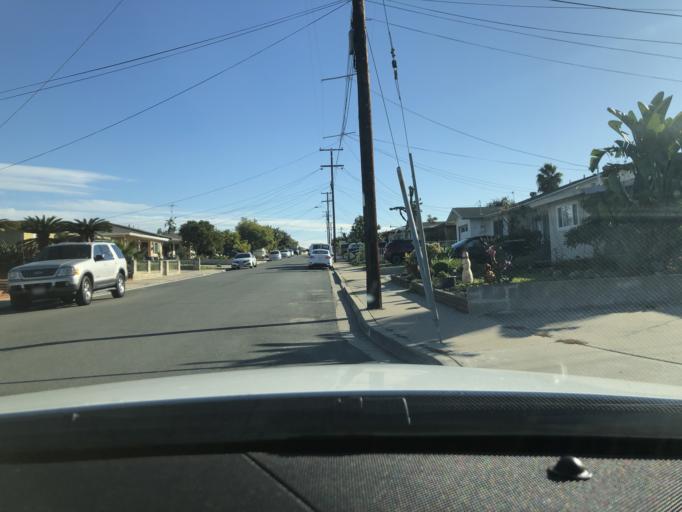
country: US
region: California
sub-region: San Diego County
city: Lemon Grove
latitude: 32.7498
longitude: -117.0636
